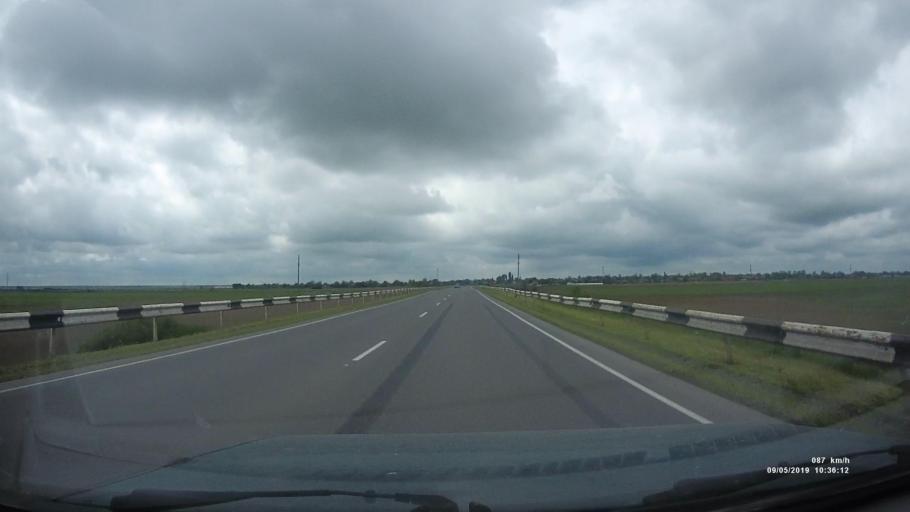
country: RU
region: Rostov
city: Peshkovo
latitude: 47.0325
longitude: 39.4097
